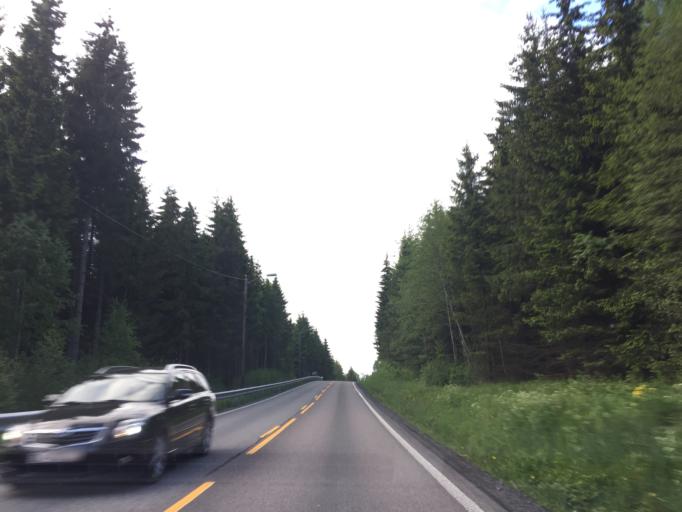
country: NO
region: Akershus
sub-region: Sorum
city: Sorumsand
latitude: 59.9551
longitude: 11.2033
